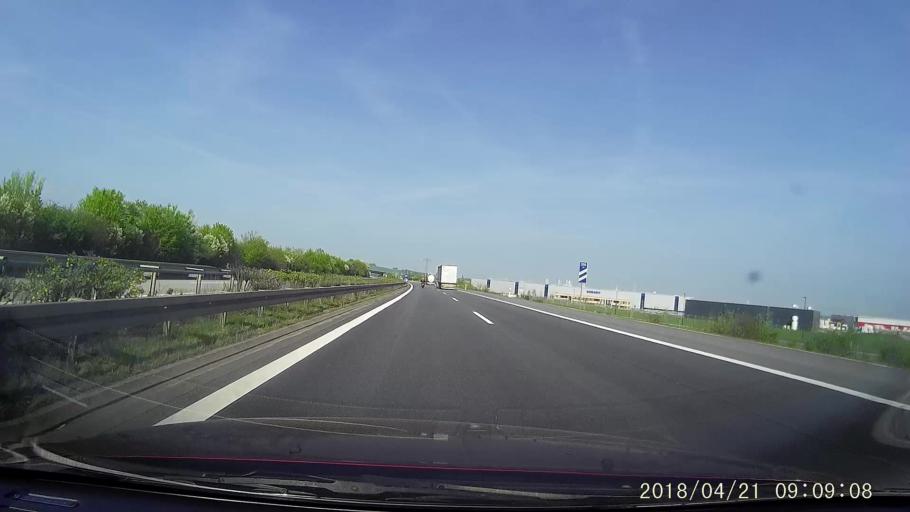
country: DE
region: Saxony
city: Kodersdorf
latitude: 51.2212
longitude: 14.9198
